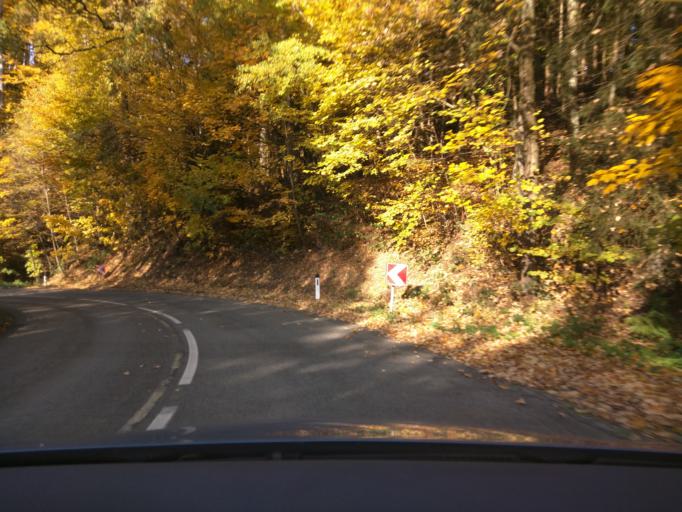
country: DE
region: Bavaria
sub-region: Lower Bavaria
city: Salzweg
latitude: 48.5666
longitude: 13.5000
